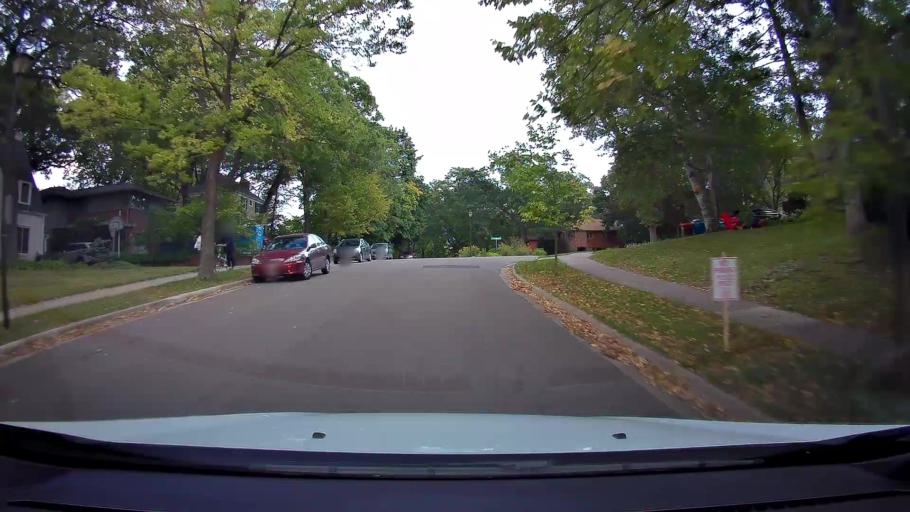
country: US
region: Minnesota
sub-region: Ramsey County
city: Lauderdale
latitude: 44.9894
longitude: -93.1953
